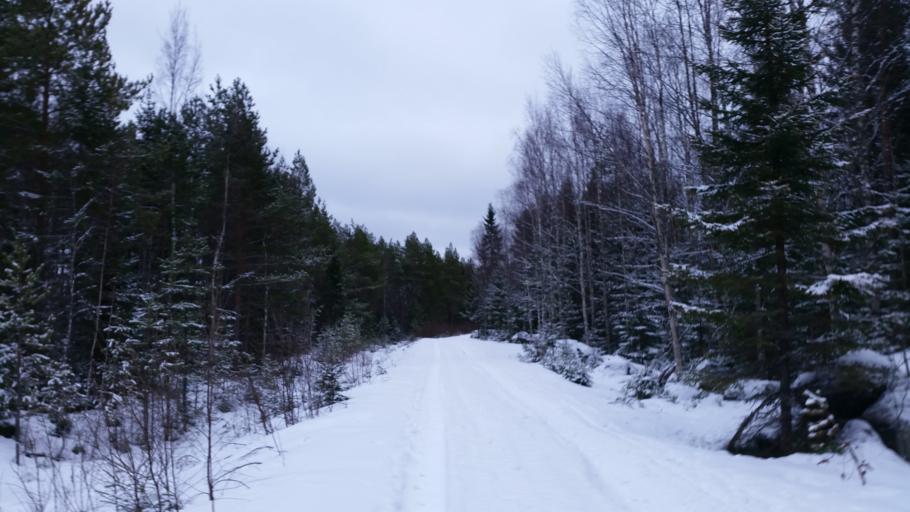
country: SE
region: Vaesterbotten
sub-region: Umea Kommun
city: Saevar
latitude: 63.9178
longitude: 20.7781
